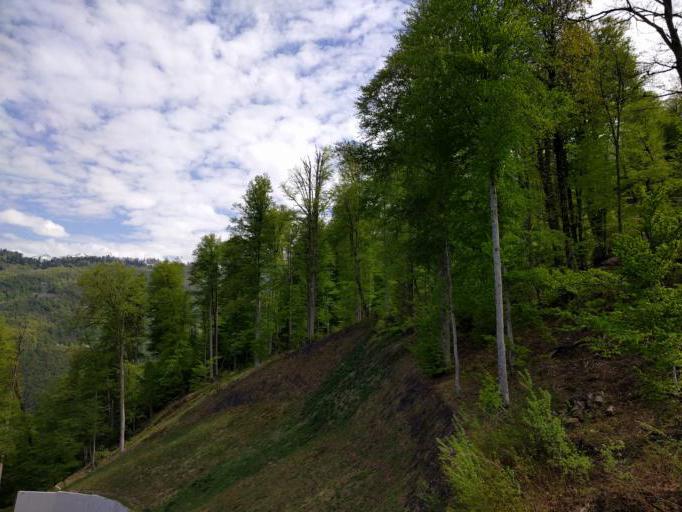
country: RU
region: Krasnodarskiy
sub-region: Sochi City
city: Krasnaya Polyana
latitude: 43.6641
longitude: 40.3104
